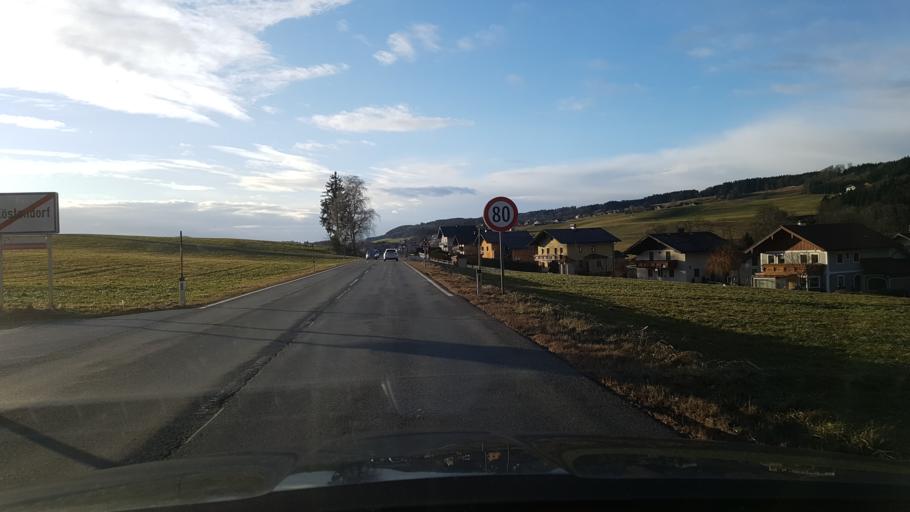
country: AT
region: Salzburg
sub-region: Politischer Bezirk Salzburg-Umgebung
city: Kostendorf
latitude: 47.9560
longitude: 13.1958
